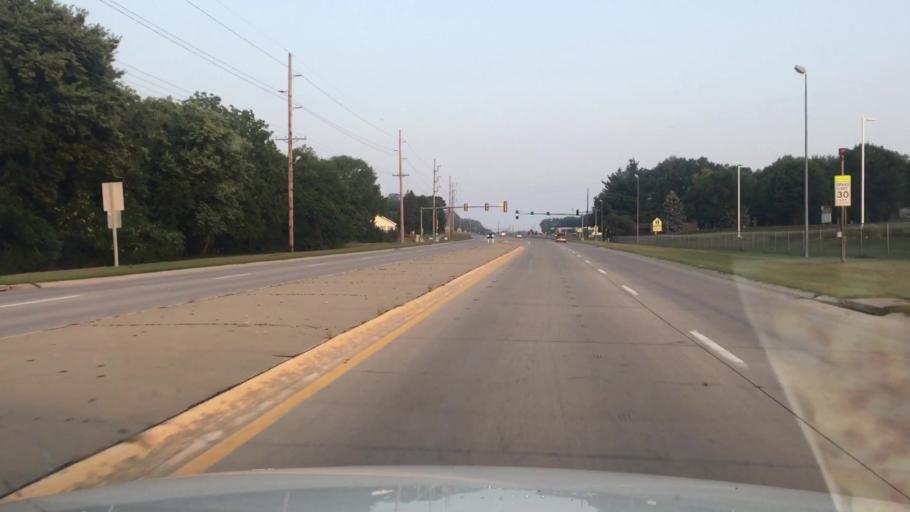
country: US
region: Iowa
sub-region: Warren County
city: Carlisle
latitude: 41.4954
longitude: -93.4894
